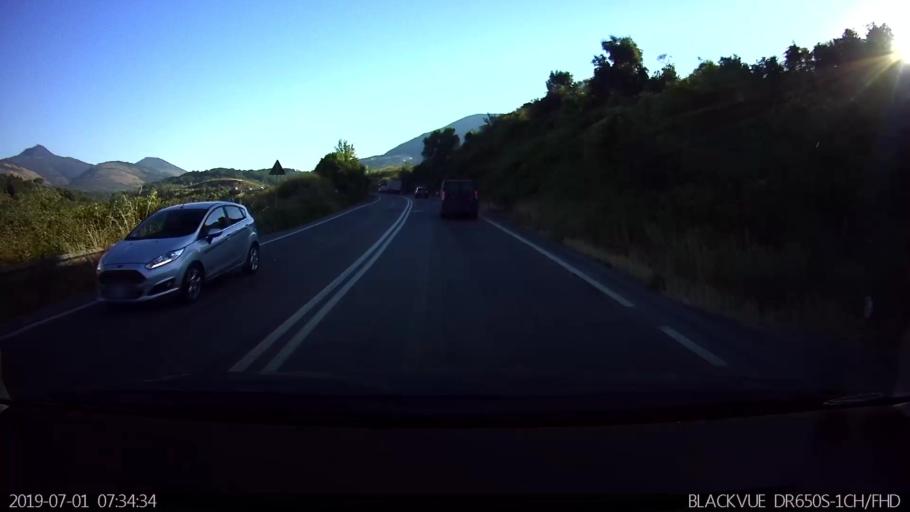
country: IT
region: Latium
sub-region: Provincia di Latina
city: Prossedi
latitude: 41.5170
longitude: 13.2726
